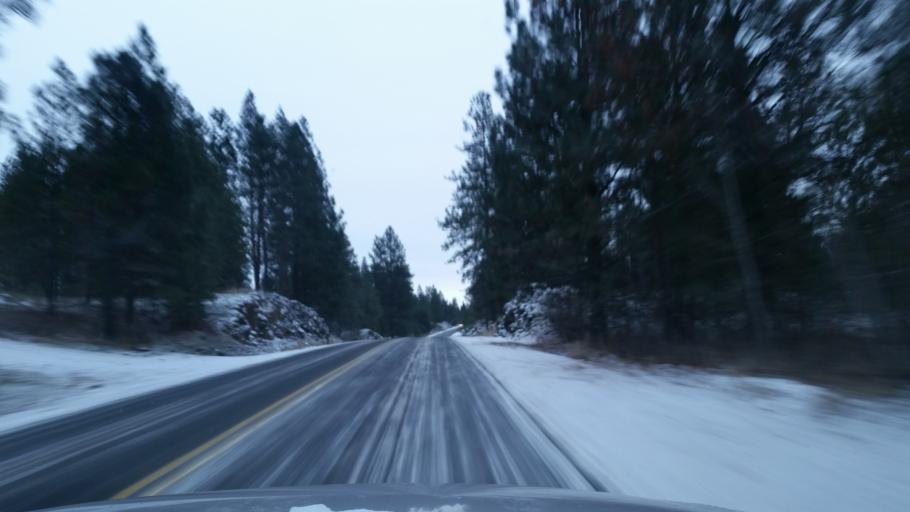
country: US
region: Washington
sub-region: Spokane County
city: Cheney
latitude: 47.4755
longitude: -117.5528
